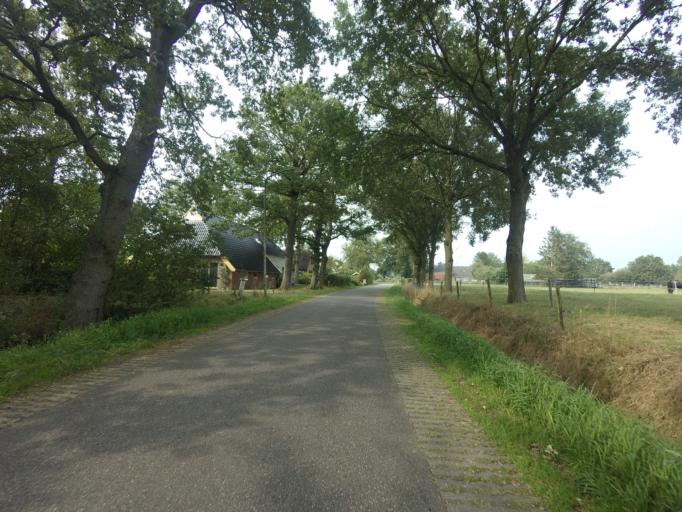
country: NL
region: Drenthe
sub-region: Gemeente Tynaarlo
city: Vries
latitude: 53.1238
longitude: 6.5679
